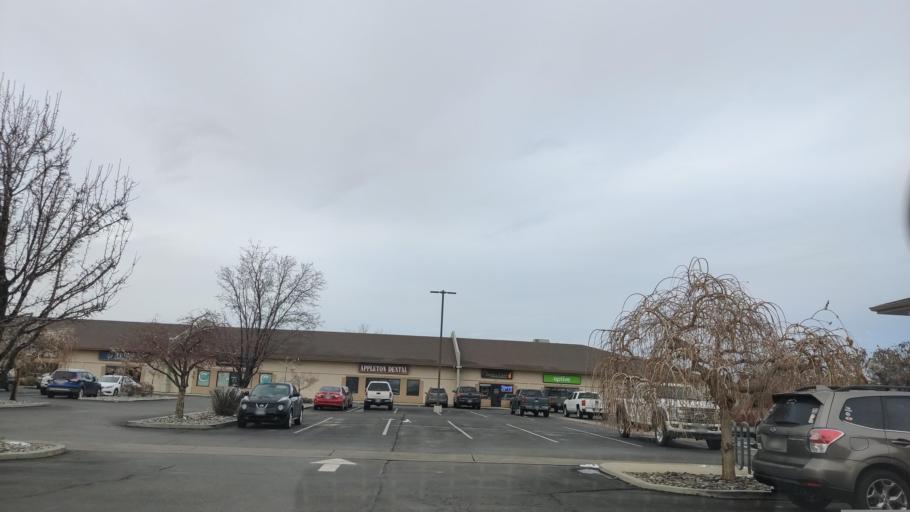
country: US
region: Colorado
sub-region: Mesa County
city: Redlands
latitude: 39.0928
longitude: -108.5936
